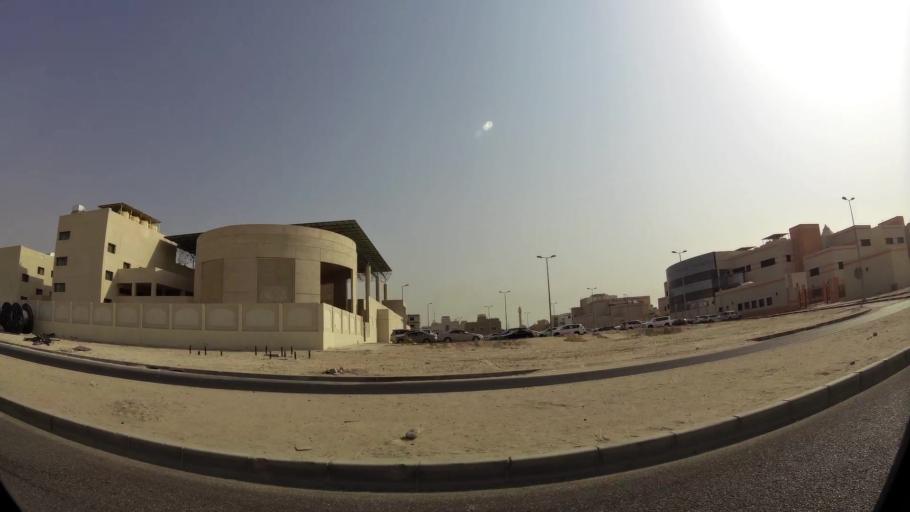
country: KW
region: Muhafazat al Jahra'
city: Al Jahra'
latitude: 29.3589
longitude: 47.7551
